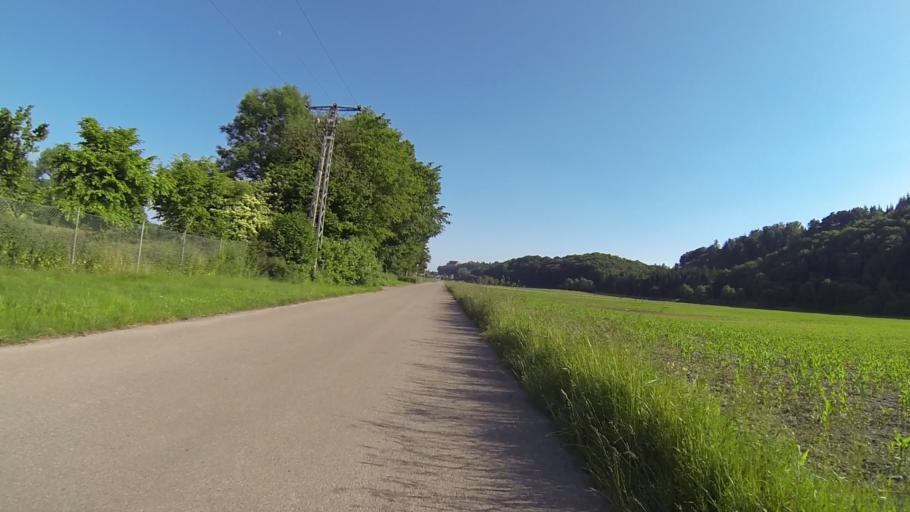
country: DE
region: Baden-Wuerttemberg
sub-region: Tuebingen Region
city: Warthausen
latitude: 48.1442
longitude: 9.7933
